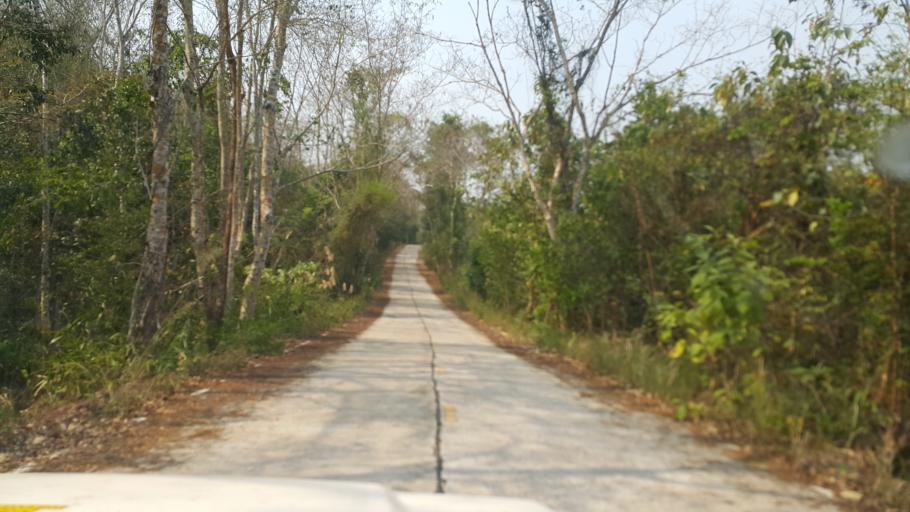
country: TH
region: Nakhon Phanom
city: Ban Phaeng
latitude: 17.9780
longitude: 104.1488
